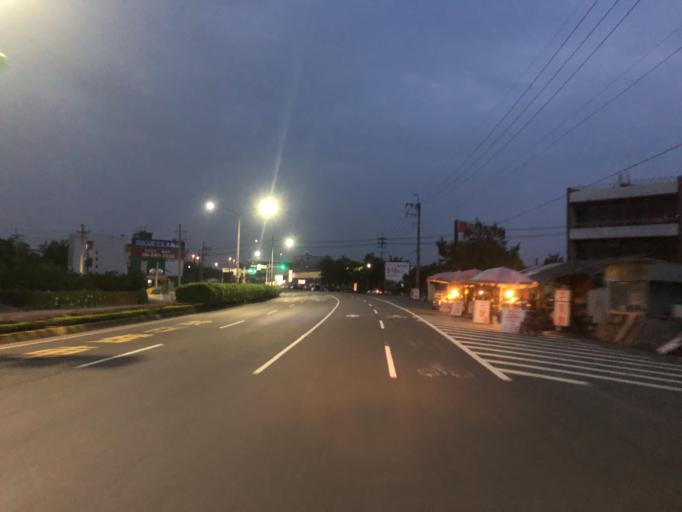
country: TW
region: Taiwan
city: Yujing
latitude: 23.1594
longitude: 120.3406
